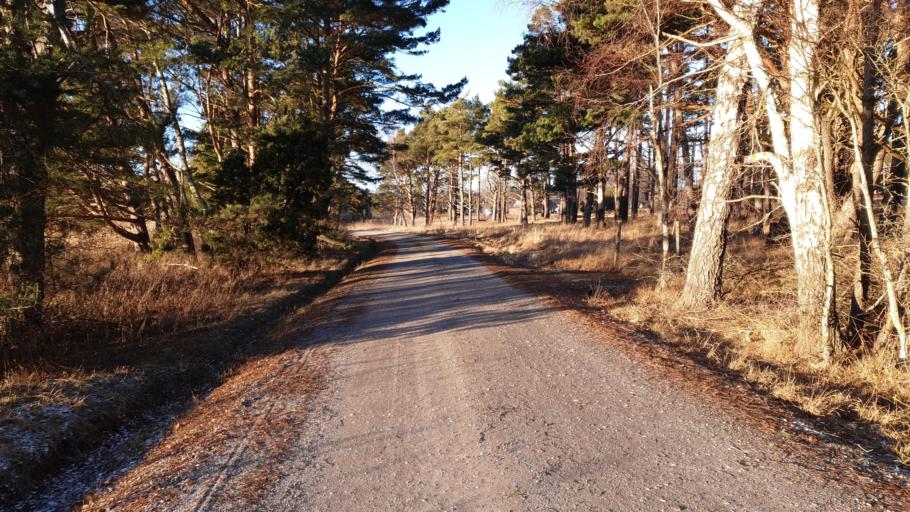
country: SE
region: Gotland
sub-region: Gotland
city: Slite
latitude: 57.3732
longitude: 18.8053
